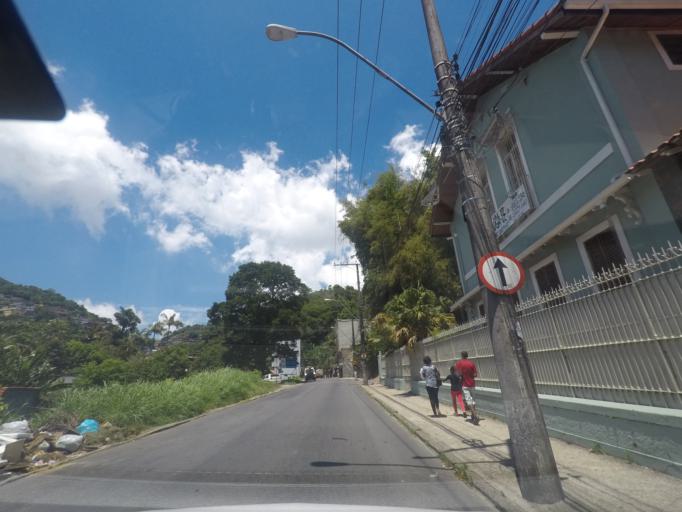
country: BR
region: Rio de Janeiro
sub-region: Petropolis
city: Petropolis
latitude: -22.5125
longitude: -43.1727
